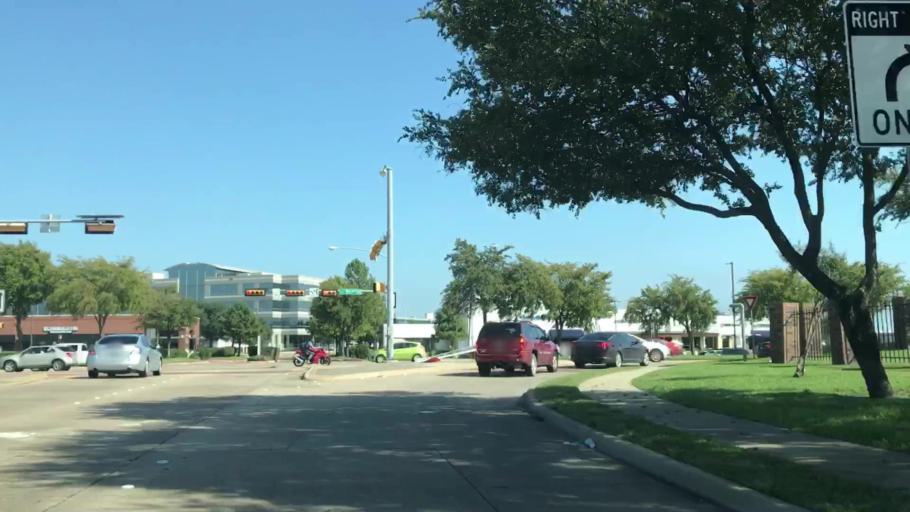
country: US
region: Texas
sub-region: Dallas County
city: Farmers Branch
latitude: 32.9070
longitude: -96.9593
